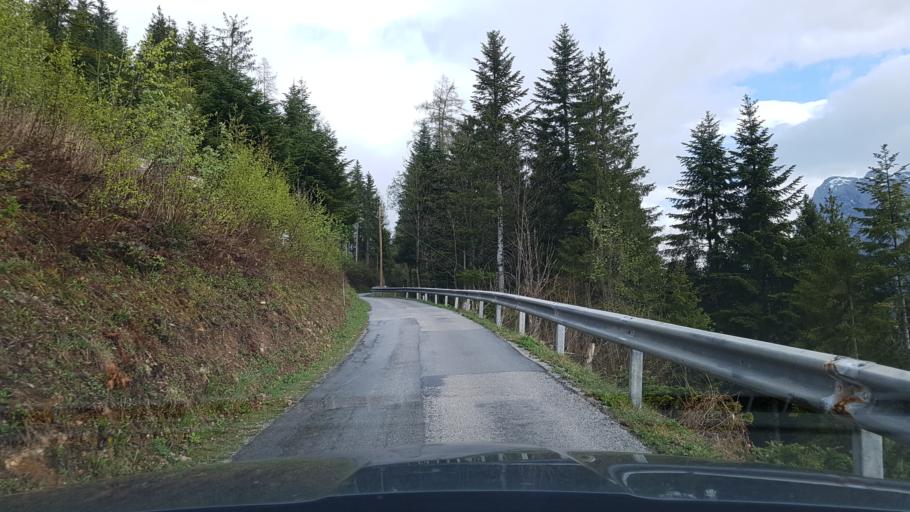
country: AT
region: Salzburg
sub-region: Politischer Bezirk Sankt Johann im Pongau
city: Werfen
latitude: 47.4636
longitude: 13.1788
